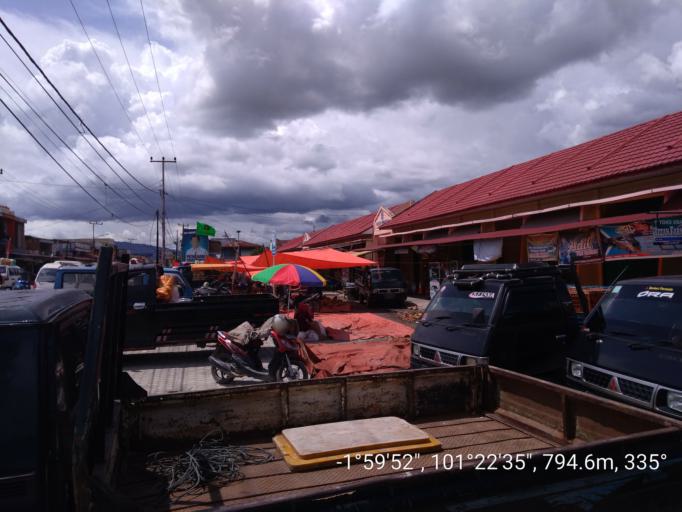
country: ID
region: Jambi
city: Semurup
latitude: -1.9979
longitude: 101.3766
